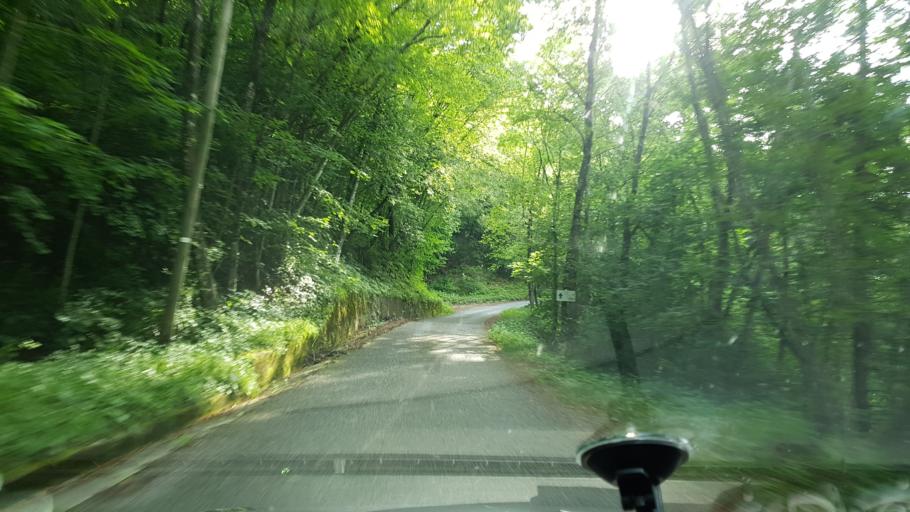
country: IT
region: Friuli Venezia Giulia
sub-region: Provincia di Udine
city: Prato
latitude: 46.3527
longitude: 13.3826
